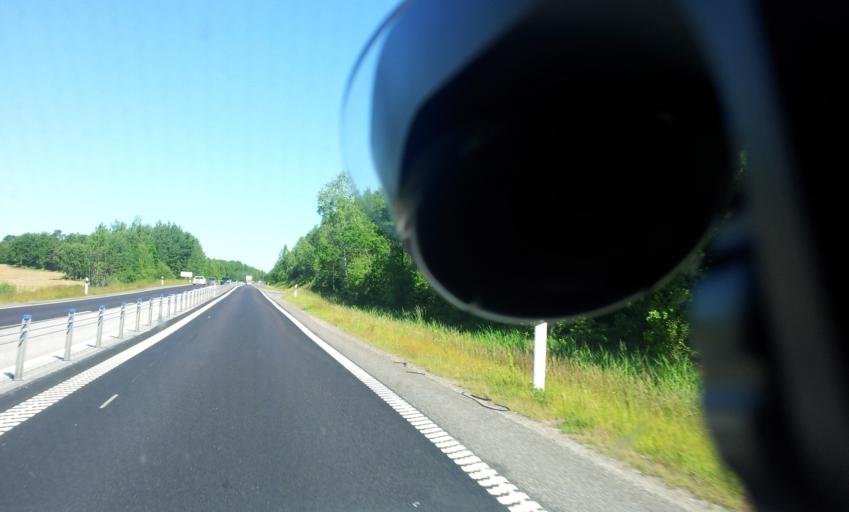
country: SE
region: OEstergoetland
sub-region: Soderkopings Kommun
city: Soederkoeping
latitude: 58.5038
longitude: 16.2987
